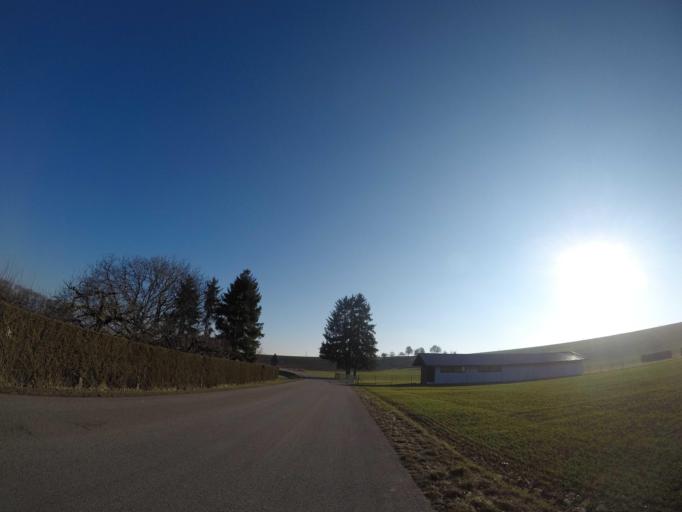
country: DE
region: Baden-Wuerttemberg
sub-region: Tuebingen Region
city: Bernstadt
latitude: 48.4793
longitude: 10.0693
